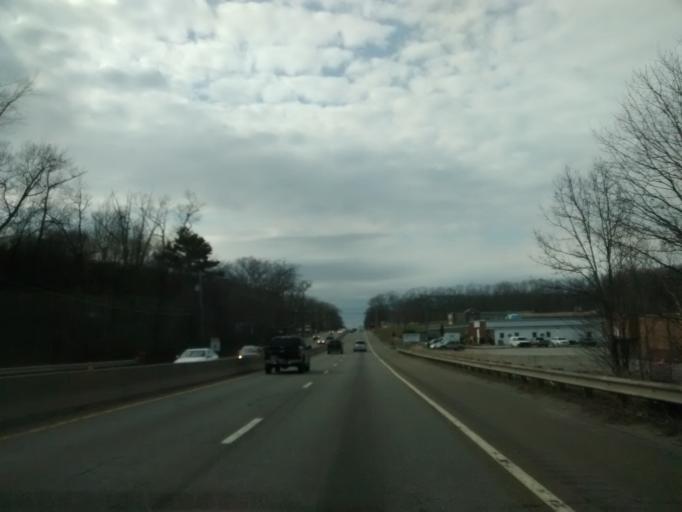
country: US
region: Massachusetts
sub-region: Worcester County
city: Sutton
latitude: 42.1677
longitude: -71.7472
